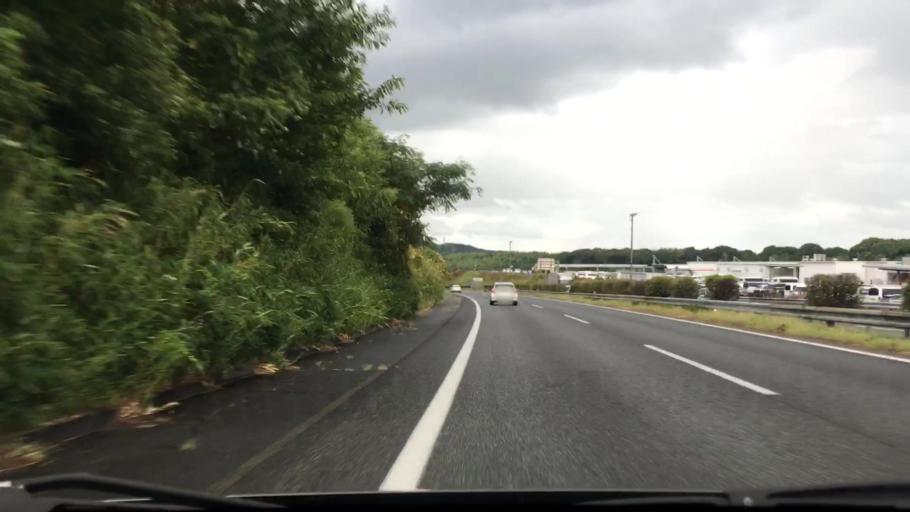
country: JP
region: Fukuoka
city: Miyata
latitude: 33.7449
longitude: 130.6199
